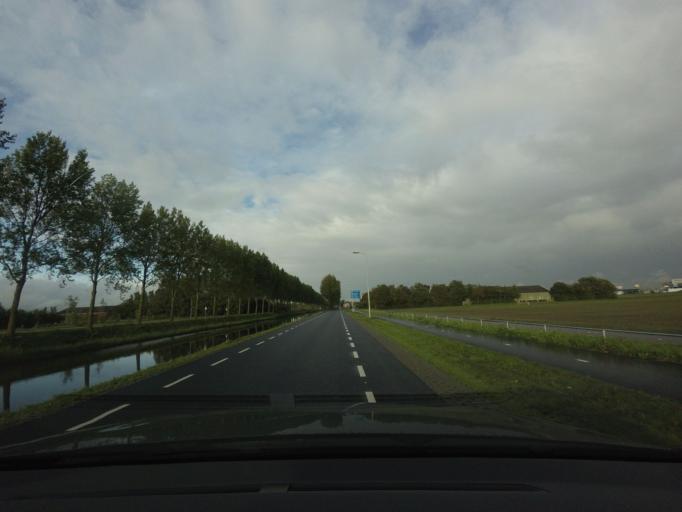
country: NL
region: South Holland
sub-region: Gemeente Kaag en Braassem
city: Oude Wetering
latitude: 52.2531
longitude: 4.6179
